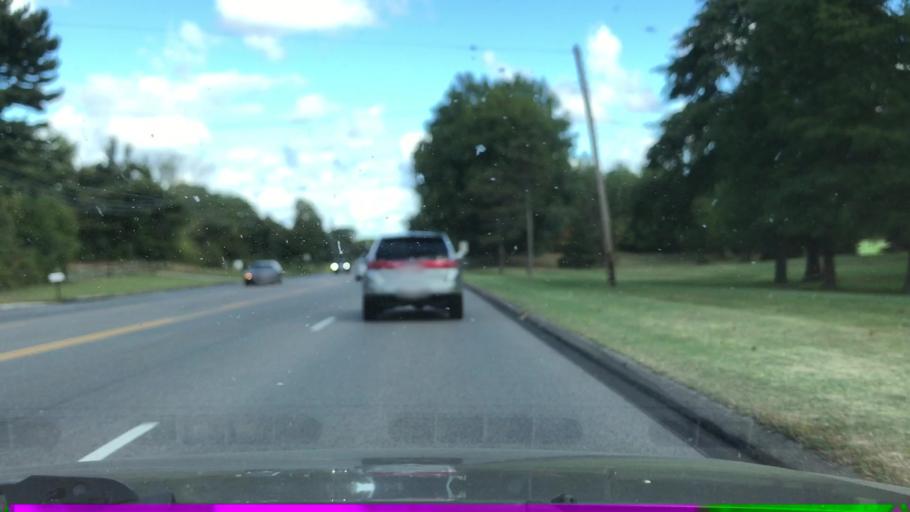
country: US
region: Ohio
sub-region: Lake County
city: Wickliffe
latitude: 41.5906
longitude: -81.4396
